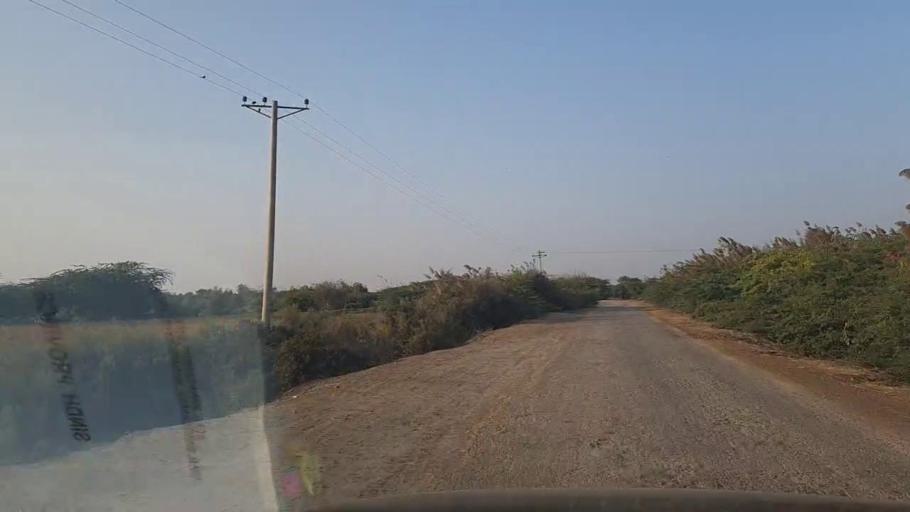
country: PK
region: Sindh
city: Keti Bandar
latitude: 24.2849
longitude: 67.5875
